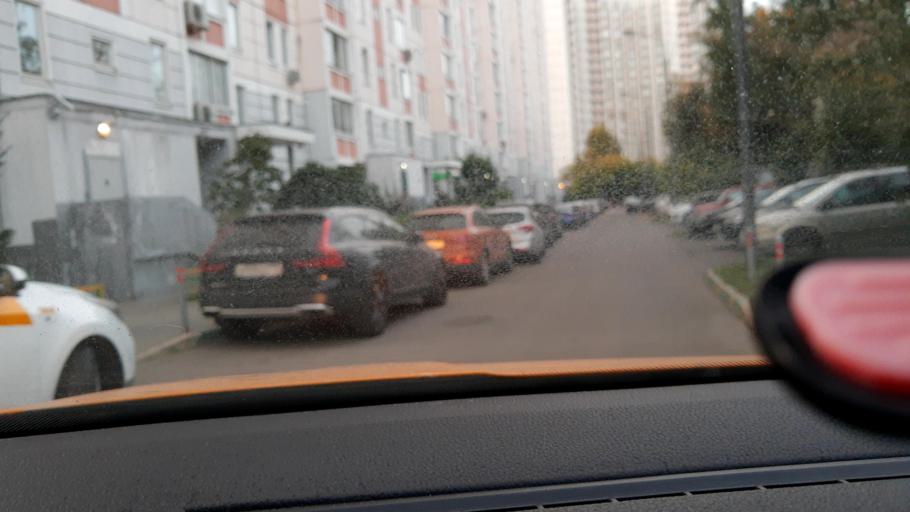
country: RU
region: Moskovskaya
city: Marfino
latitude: 55.7134
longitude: 37.3981
